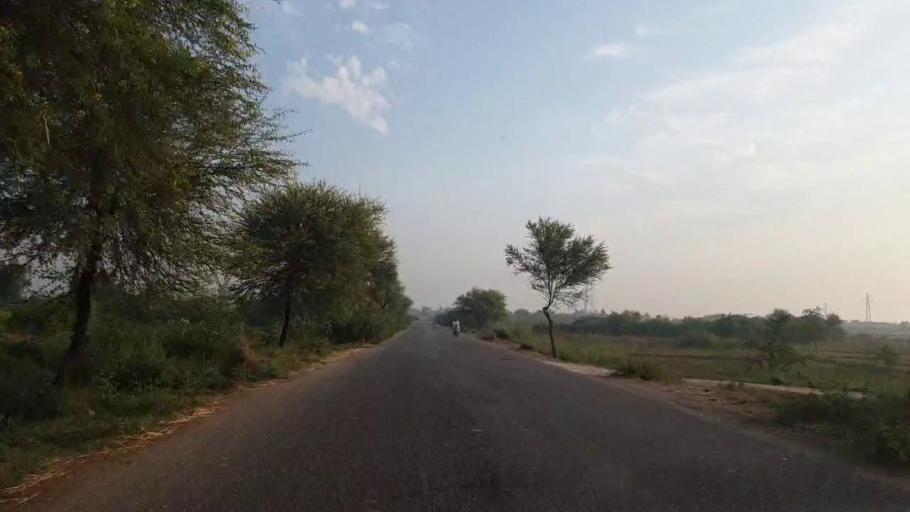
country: PK
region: Sindh
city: Tando Bago
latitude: 24.7051
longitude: 68.9280
